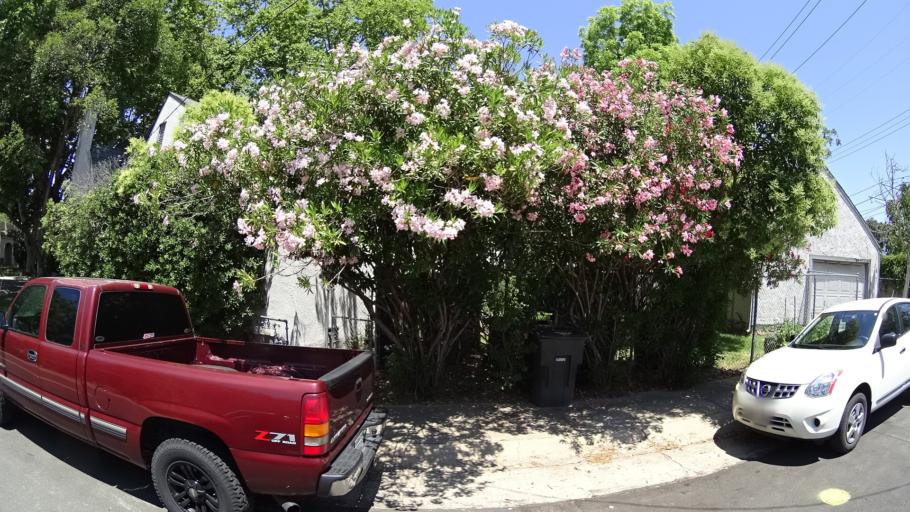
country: US
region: California
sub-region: Sacramento County
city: Sacramento
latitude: 38.5578
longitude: -121.4888
